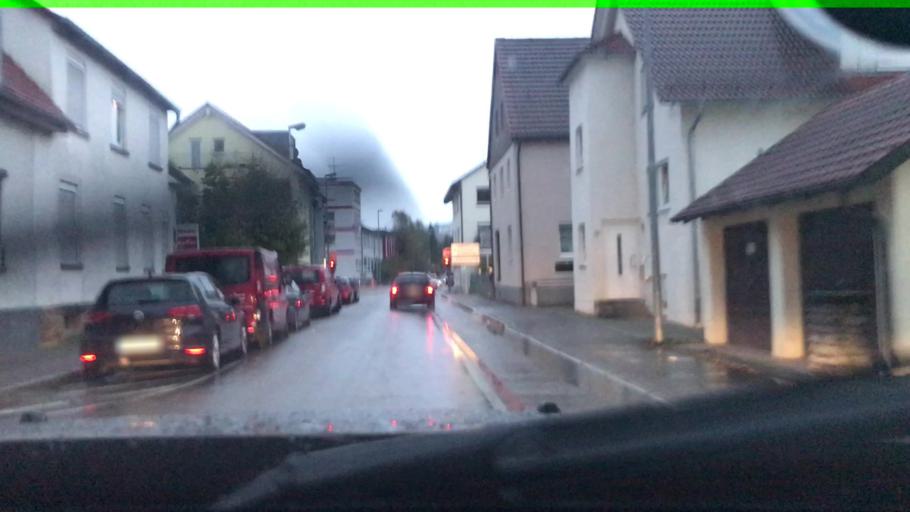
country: DE
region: Baden-Wuerttemberg
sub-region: Regierungsbezirk Stuttgart
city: Winnenden
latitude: 48.8765
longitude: 9.3938
